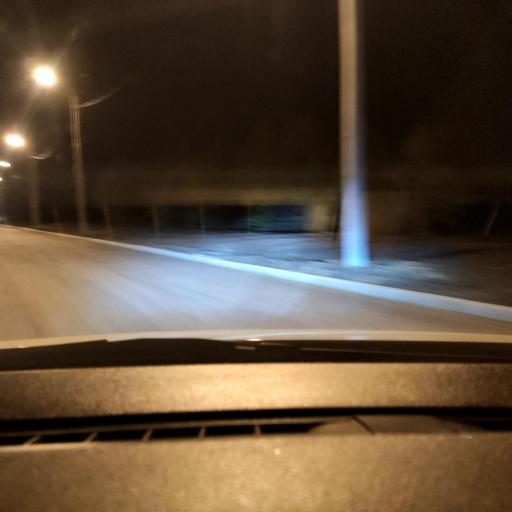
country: RU
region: Voronezj
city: Podgornoye
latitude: 51.7705
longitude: 39.1902
